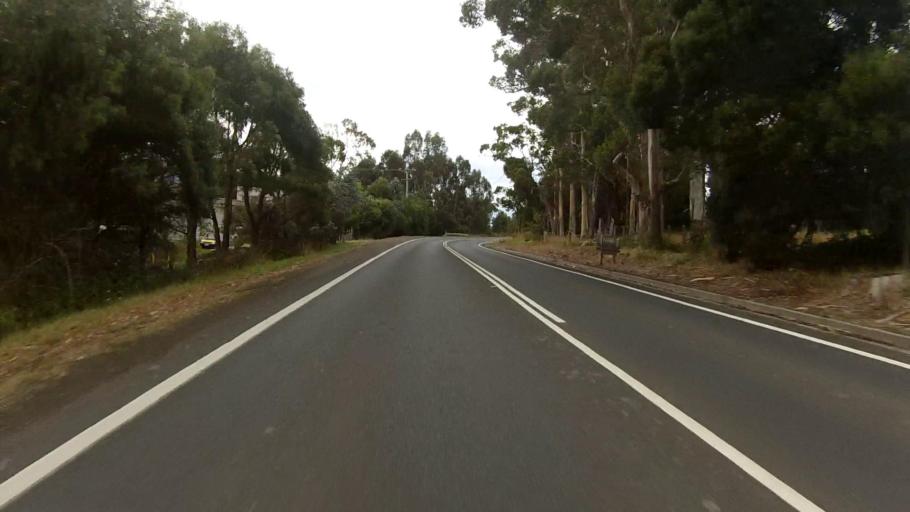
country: AU
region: Tasmania
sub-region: Huon Valley
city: Franklin
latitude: -43.0778
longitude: 147.0329
